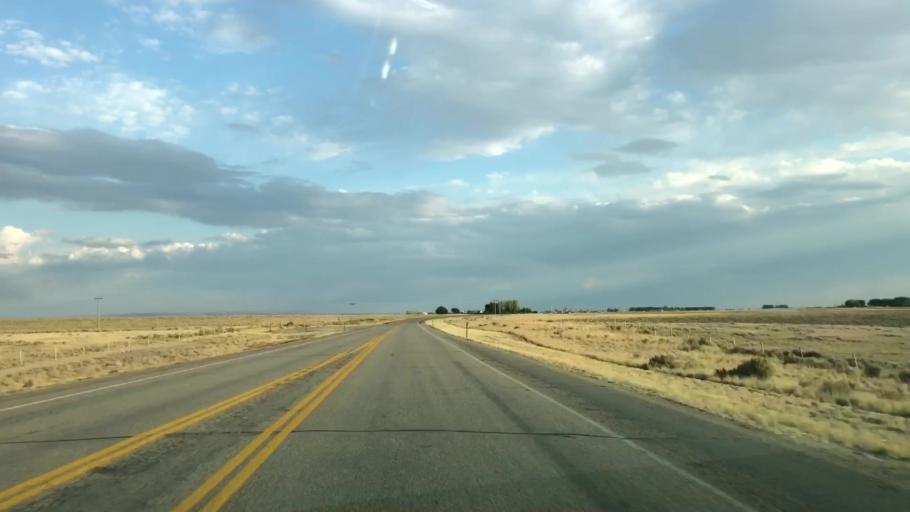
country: US
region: Wyoming
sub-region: Sweetwater County
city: North Rock Springs
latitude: 42.0888
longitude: -109.4402
